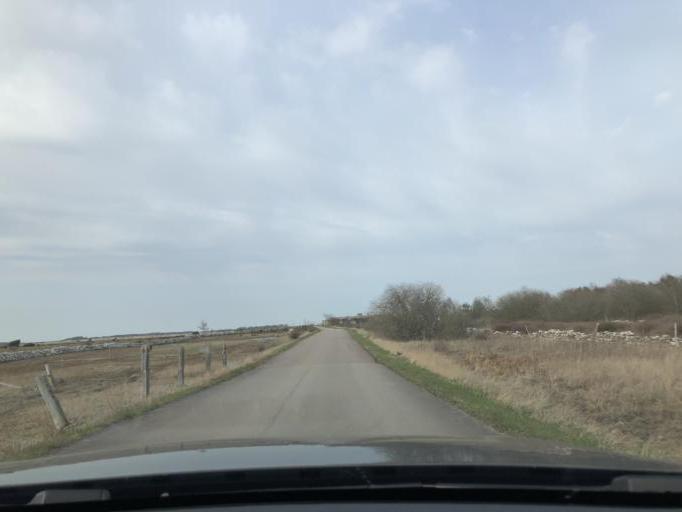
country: SE
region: Kalmar
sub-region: Morbylanga Kommun
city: Moerbylanga
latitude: 56.2904
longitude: 16.4823
